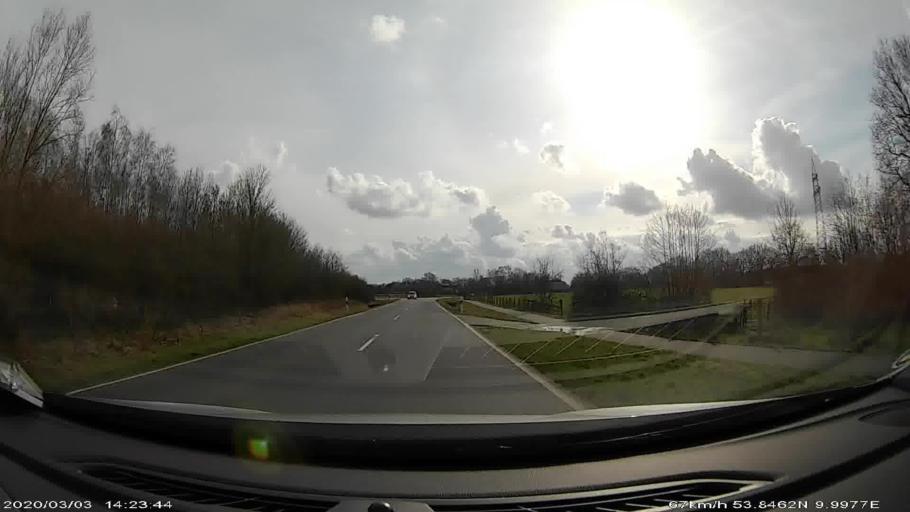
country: DE
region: Schleswig-Holstein
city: Oersdorf
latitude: 53.8461
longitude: 9.9977
